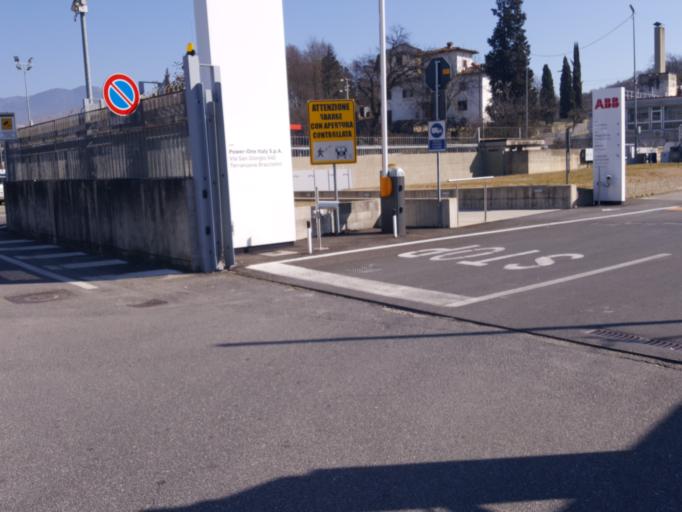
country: IT
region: Tuscany
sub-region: Province of Arezzo
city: Terranuova Bracciolini
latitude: 43.5512
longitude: 11.5914
